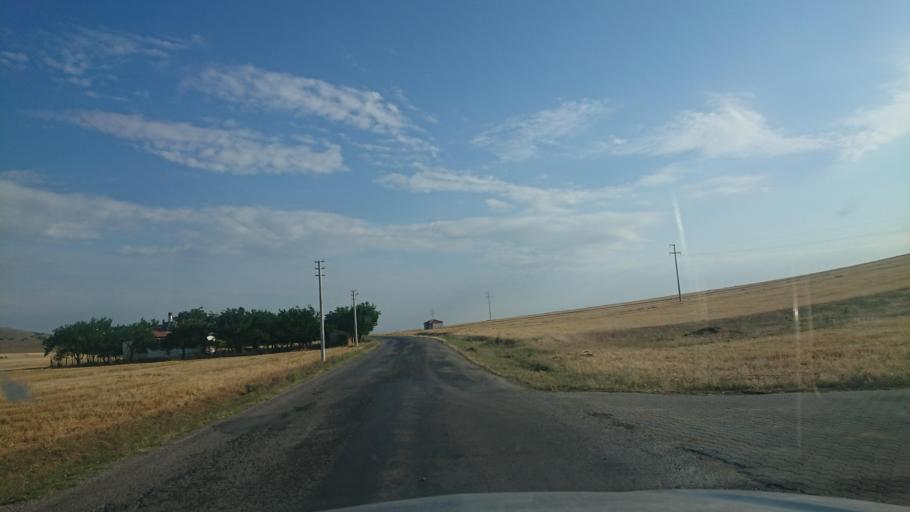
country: TR
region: Aksaray
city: Ortakoy
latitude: 38.7742
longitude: 34.0617
